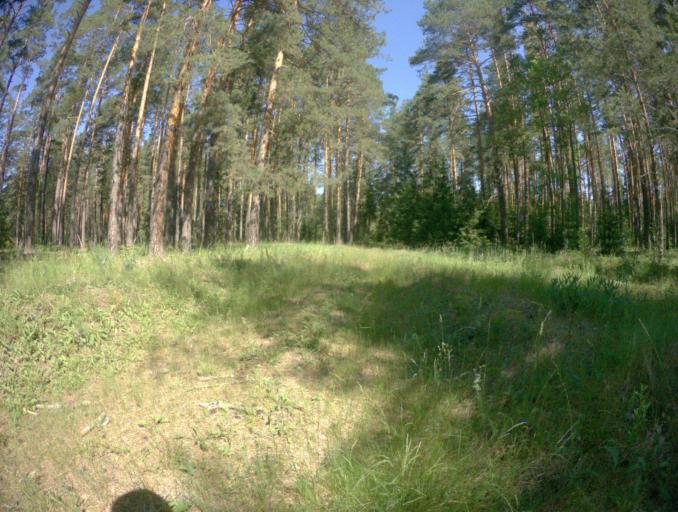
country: RU
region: Ivanovo
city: Talitsy
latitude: 56.3478
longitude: 42.3307
